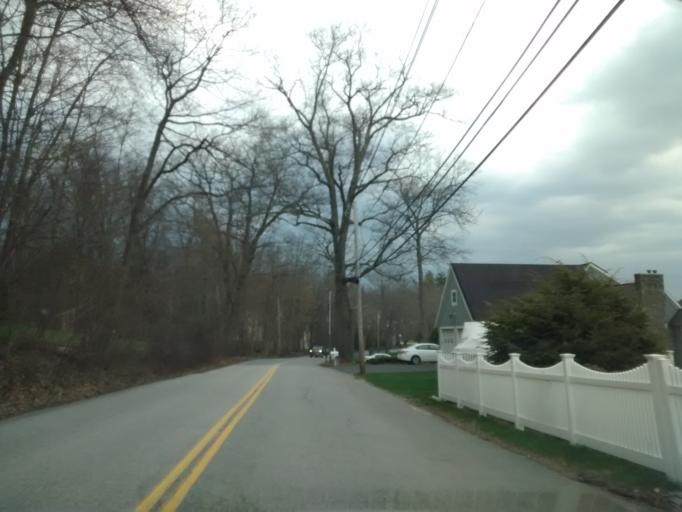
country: US
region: Massachusetts
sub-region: Worcester County
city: Sutton
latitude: 42.1671
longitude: -71.7877
